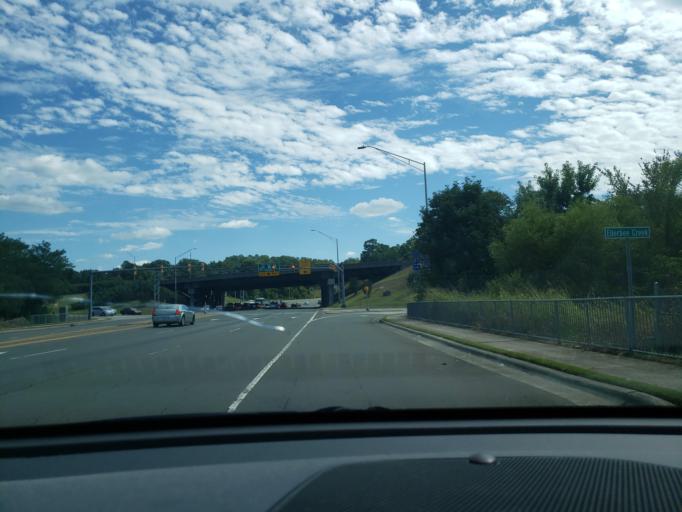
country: US
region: North Carolina
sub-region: Durham County
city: Durham
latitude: 36.0154
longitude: -78.8885
